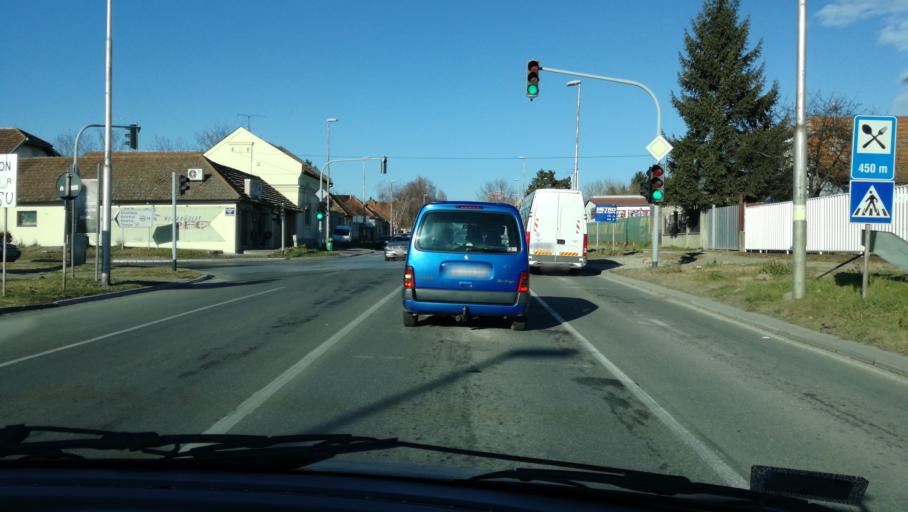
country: RS
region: Autonomna Pokrajina Vojvodina
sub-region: Severnobacki Okrug
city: Subotica
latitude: 46.0874
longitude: 19.6844
